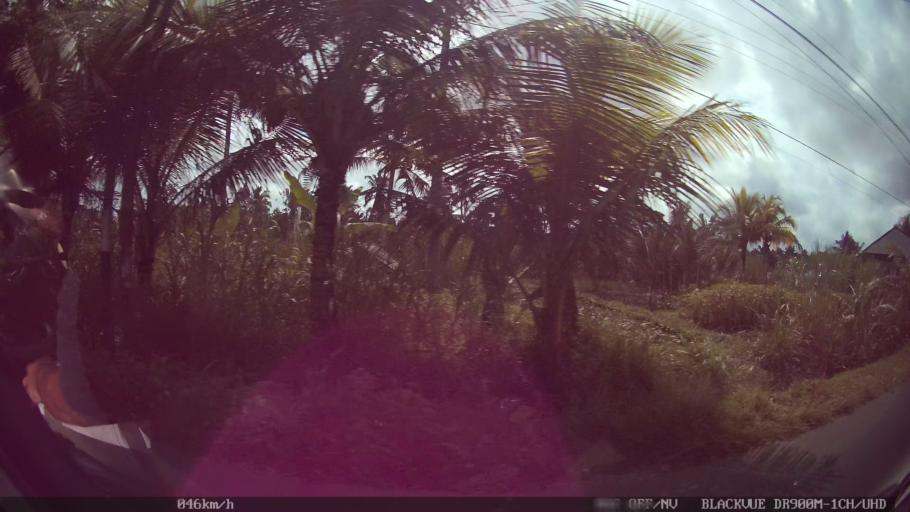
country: ID
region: Bali
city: Banjar Madangan Kaja
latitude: -8.4862
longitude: 115.3213
